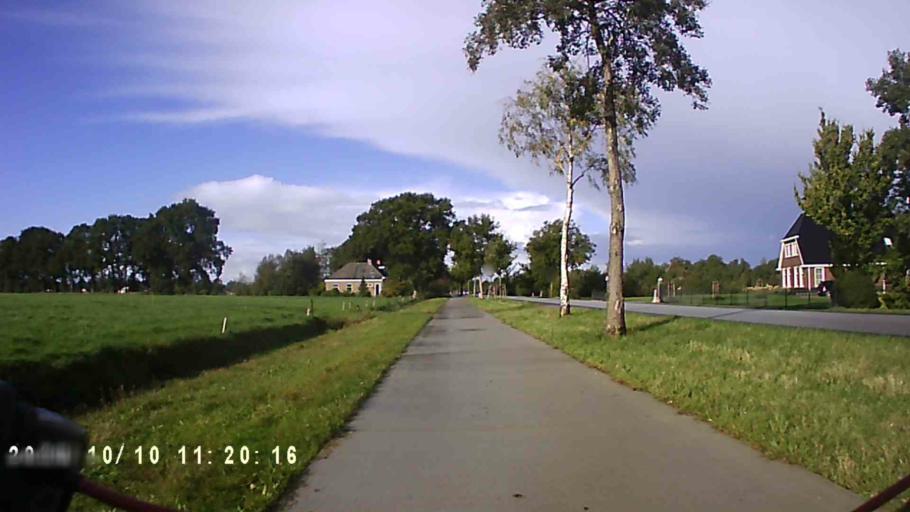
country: NL
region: Friesland
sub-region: Gemeente Smallingerland
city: Drachtstercompagnie
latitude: 53.0950
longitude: 6.1869
